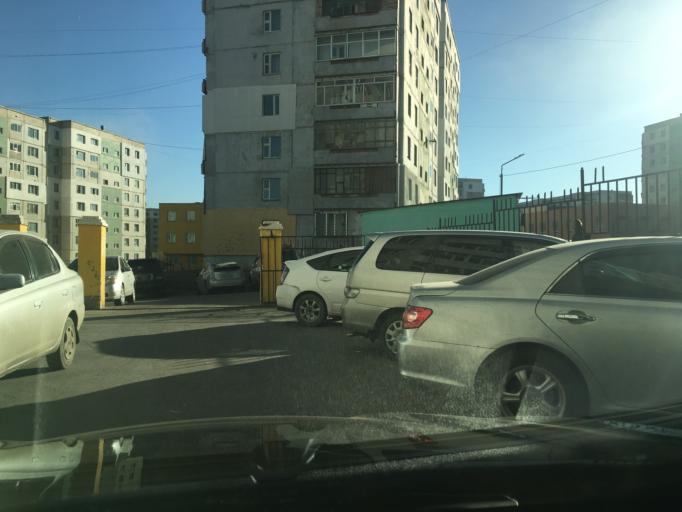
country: MN
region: Ulaanbaatar
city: Ulaanbaatar
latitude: 47.9281
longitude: 106.8814
